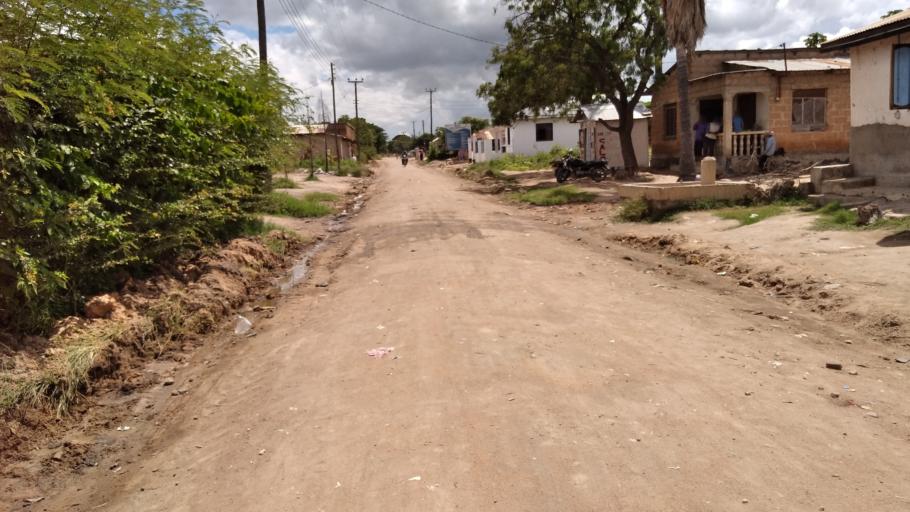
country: TZ
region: Dodoma
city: Dodoma
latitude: -6.1634
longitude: 35.7397
